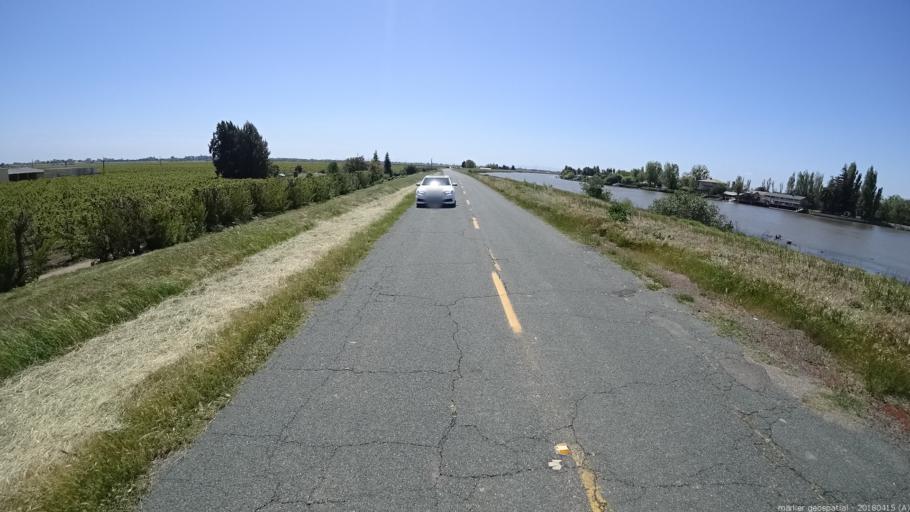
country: US
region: California
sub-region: Solano County
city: Rio Vista
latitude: 38.2049
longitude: -121.6097
